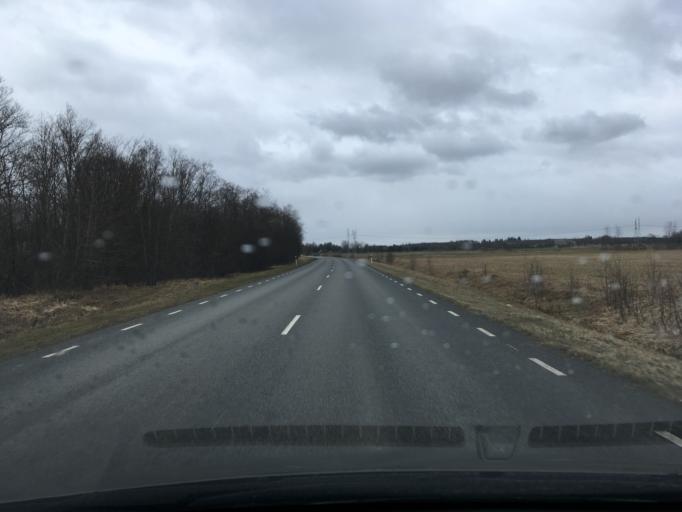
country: EE
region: Laeaene
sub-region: Lihula vald
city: Lihula
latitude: 58.6602
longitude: 23.8362
